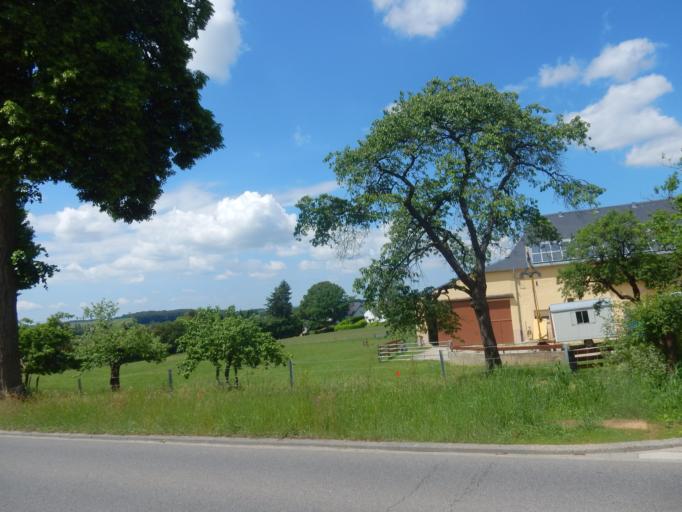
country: LU
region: Luxembourg
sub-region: Canton de Mersch
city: Tuntange
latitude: 49.7363
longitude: 6.0234
